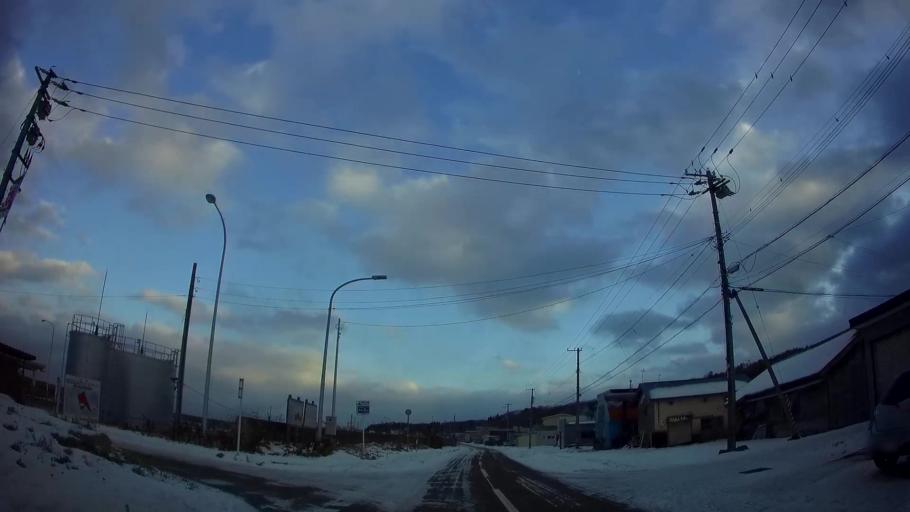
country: JP
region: Hokkaido
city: Nanae
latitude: 42.0337
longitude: 140.8217
